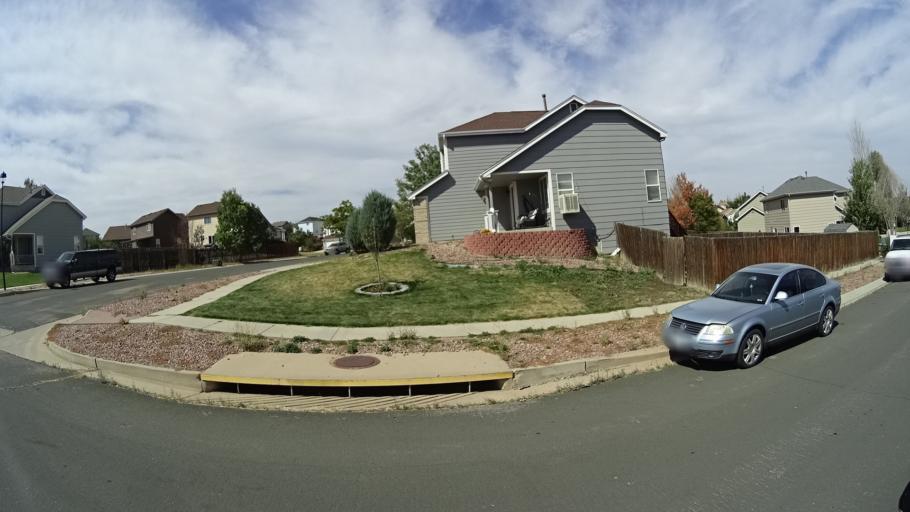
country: US
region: Colorado
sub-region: El Paso County
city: Cimarron Hills
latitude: 38.8982
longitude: -104.7123
